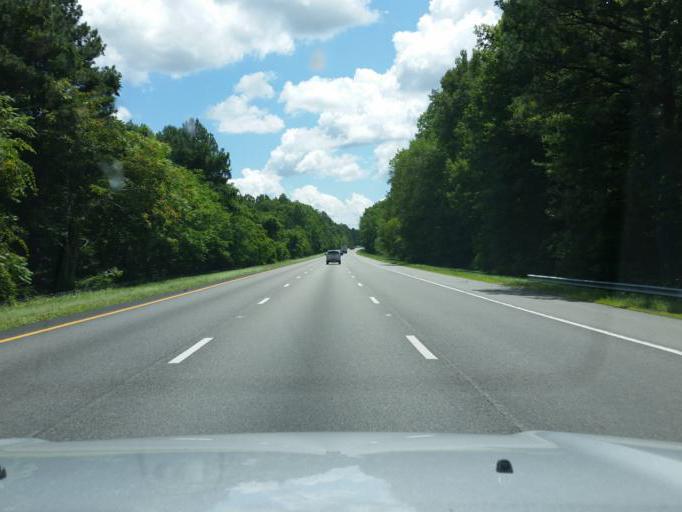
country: US
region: Virginia
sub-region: King William County
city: West Point
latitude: 37.4192
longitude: -76.8174
